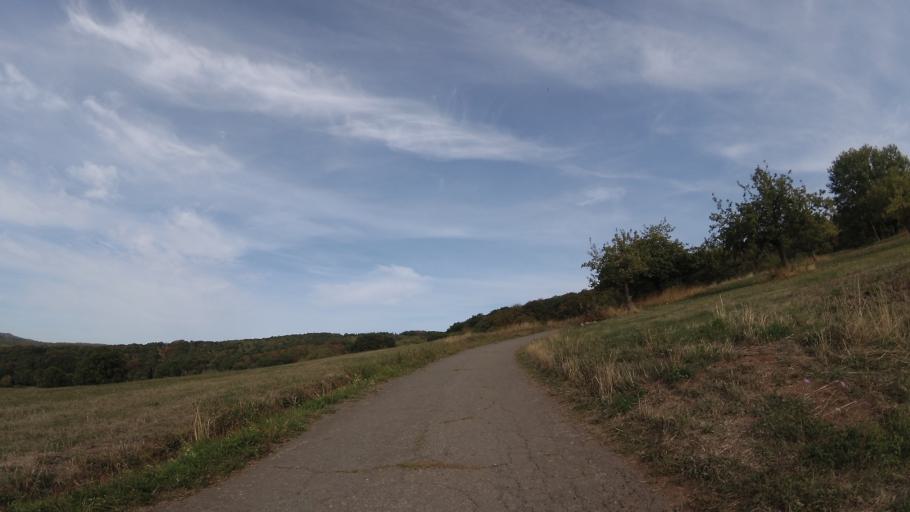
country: DE
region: Saarland
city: Sankt Wendel
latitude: 49.4758
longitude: 7.1855
